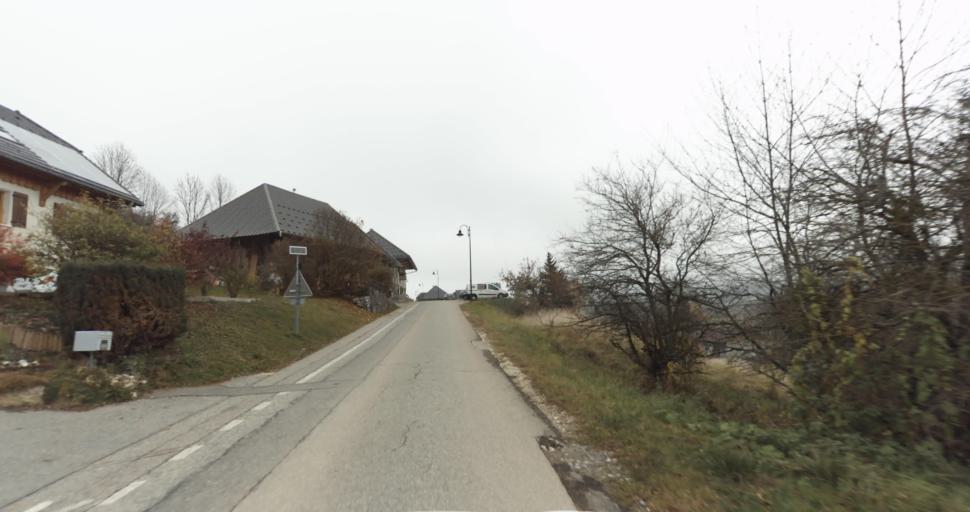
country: FR
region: Rhone-Alpes
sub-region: Departement de la Haute-Savoie
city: Gruffy
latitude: 45.7713
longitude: 6.1248
